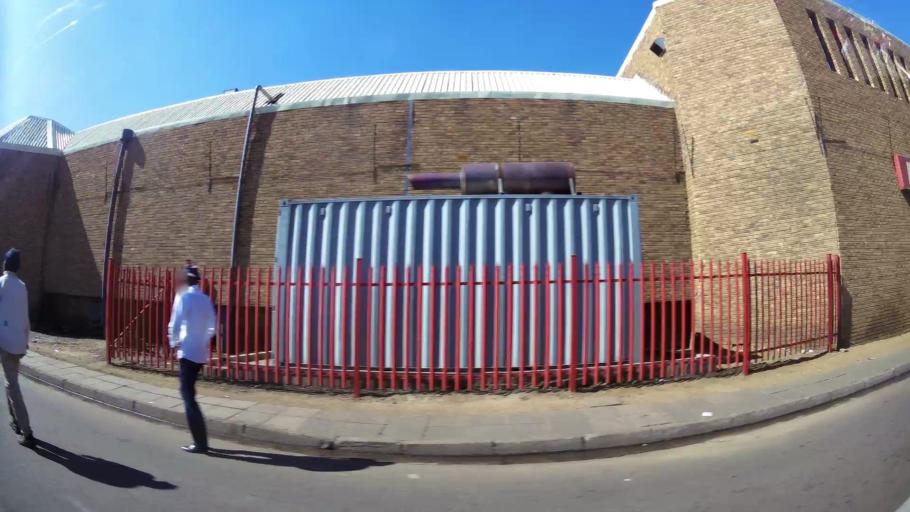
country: ZA
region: Mpumalanga
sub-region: Nkangala District Municipality
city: Witbank
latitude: -25.8753
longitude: 29.2105
